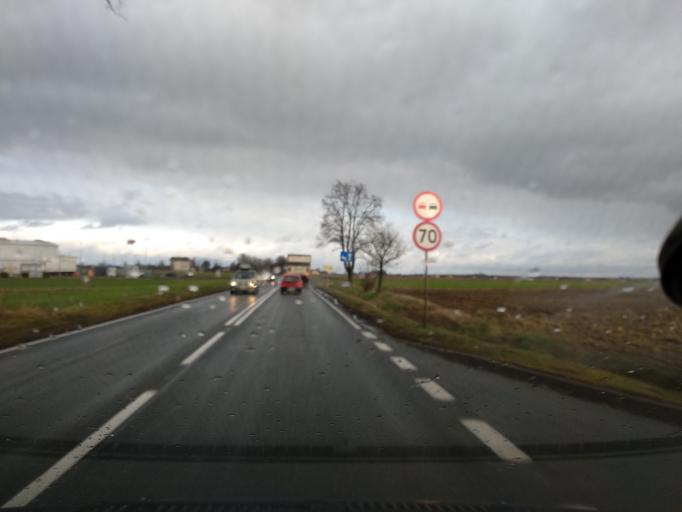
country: PL
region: Greater Poland Voivodeship
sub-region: Powiat koninski
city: Stare Miasto
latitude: 52.1462
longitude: 18.1978
